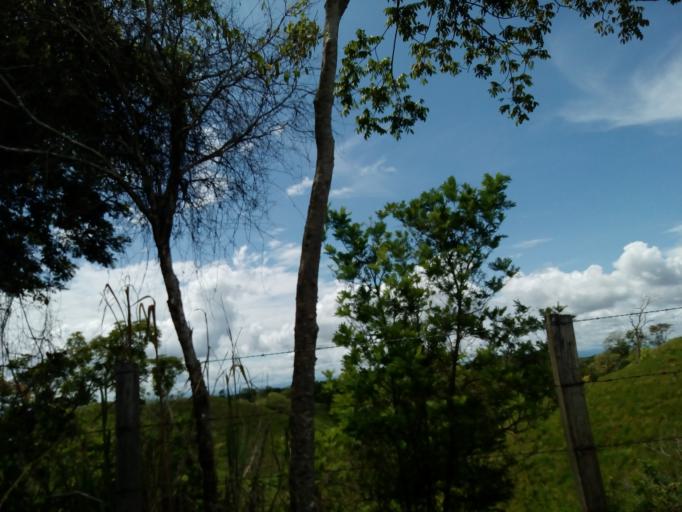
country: CO
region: Boyaca
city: Puerto Boyaca
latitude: 5.9686
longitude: -74.4378
